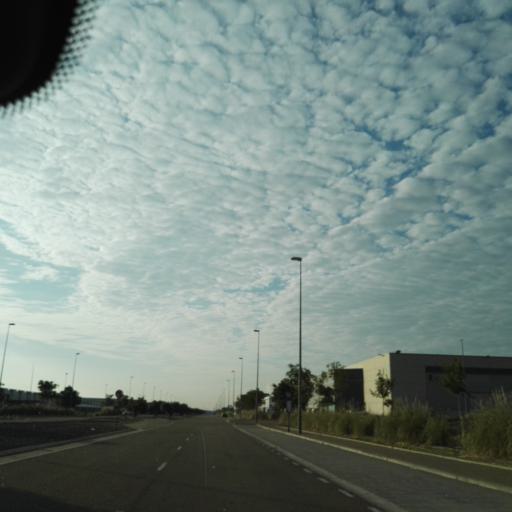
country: ES
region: Aragon
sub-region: Provincia de Zaragoza
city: Montecanal
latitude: 41.6518
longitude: -0.9956
